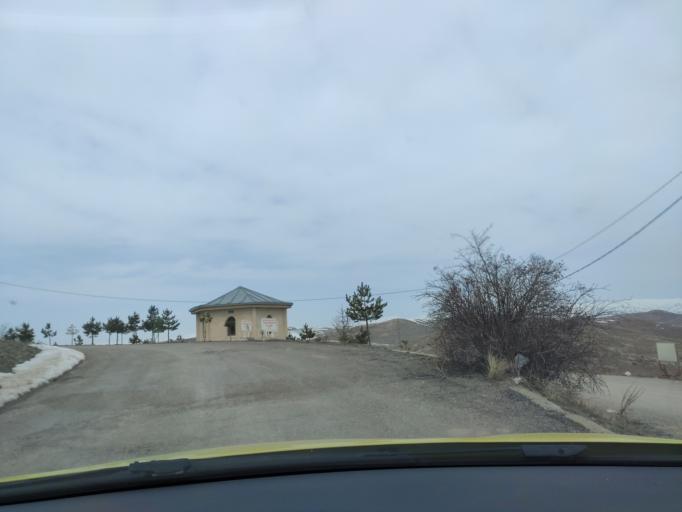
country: TR
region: Bayburt
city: Bayburt
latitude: 40.2612
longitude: 40.2205
